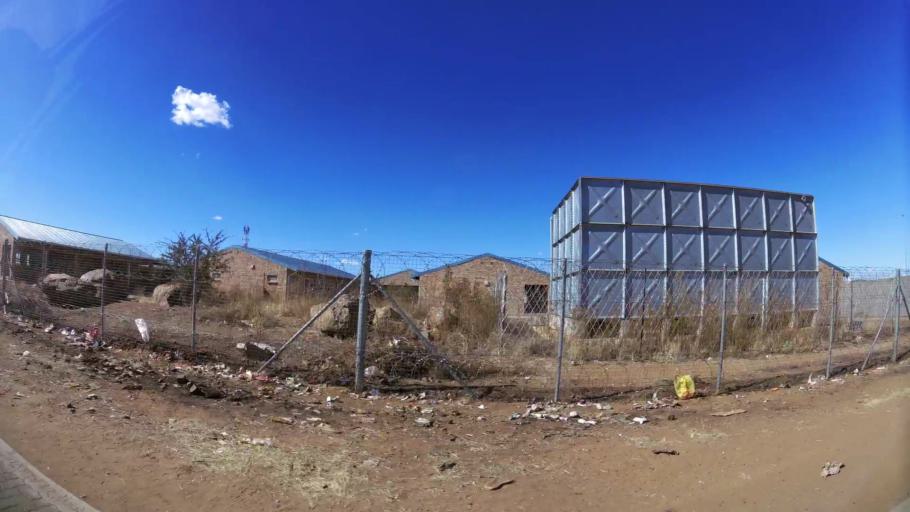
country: ZA
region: North-West
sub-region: Dr Kenneth Kaunda District Municipality
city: Klerksdorp
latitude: -26.8731
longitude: 26.5646
